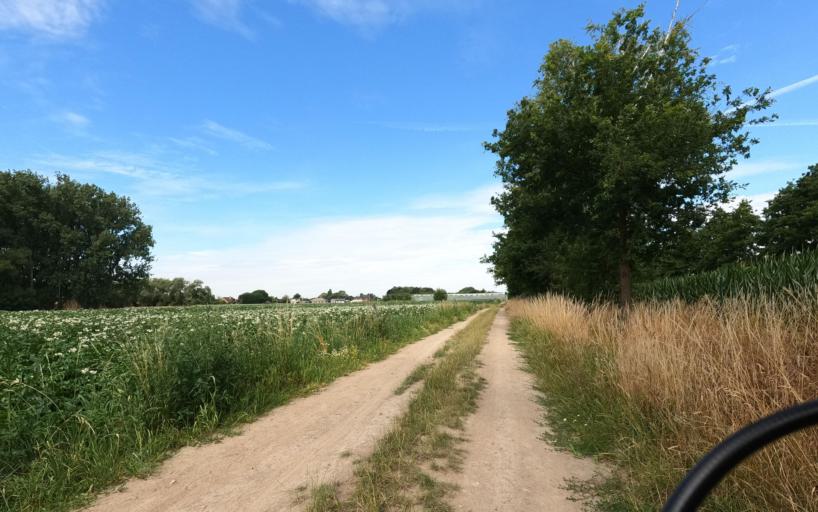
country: BE
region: Flanders
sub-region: Provincie Vlaams-Brabant
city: Kapelle-op-den-Bos
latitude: 50.9966
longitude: 4.3468
